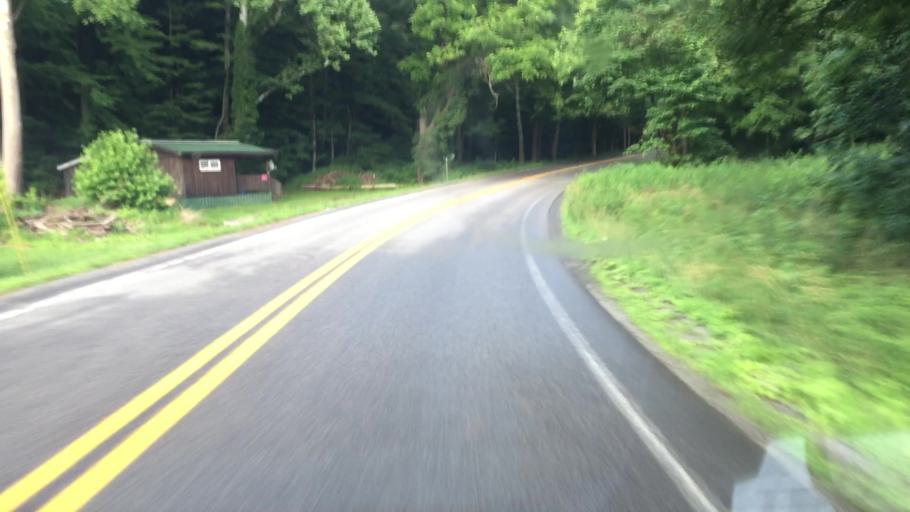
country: US
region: West Virginia
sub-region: Preston County
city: Kingwood
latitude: 39.3270
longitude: -79.8116
